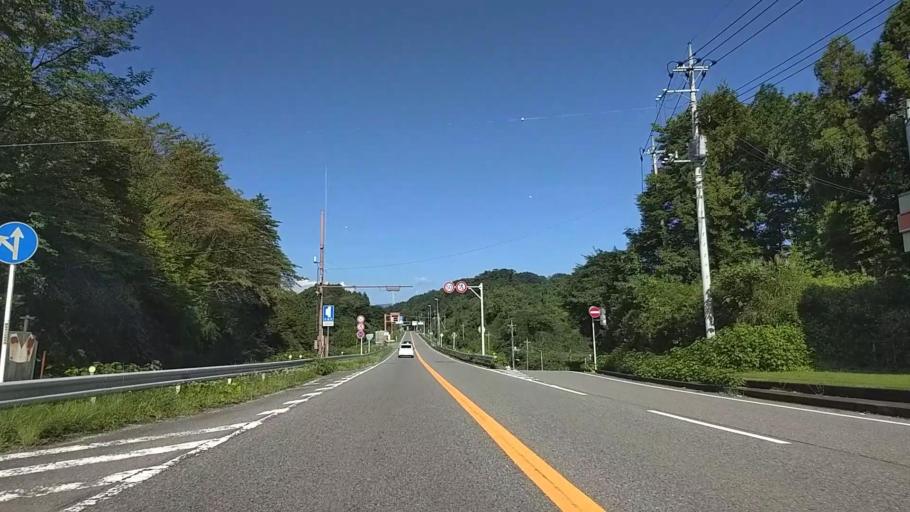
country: JP
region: Gunma
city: Annaka
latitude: 36.3140
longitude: 138.8084
